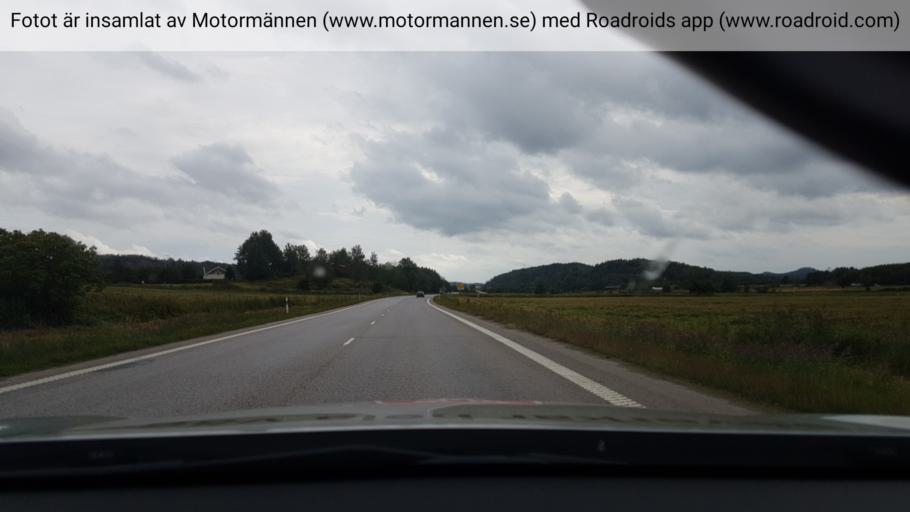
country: SE
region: Vaestra Goetaland
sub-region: Munkedals Kommun
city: Munkedal
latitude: 58.5078
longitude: 11.5755
